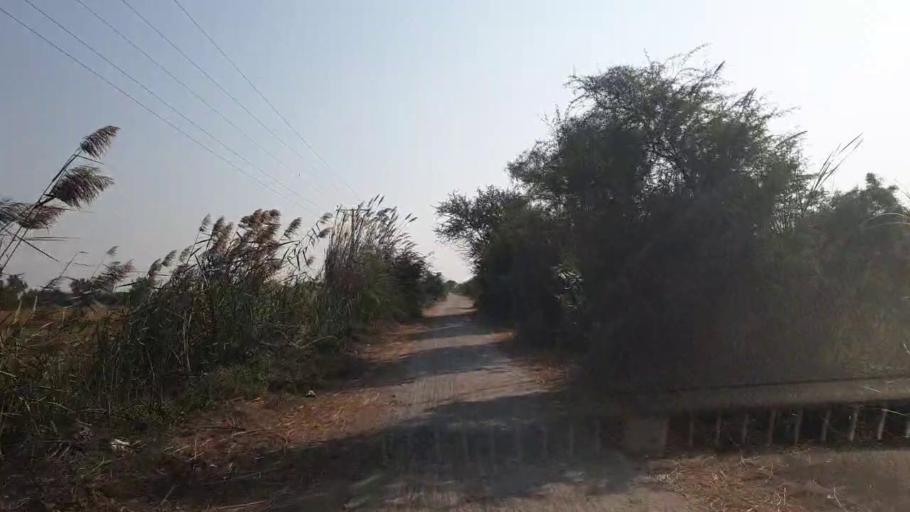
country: PK
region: Sindh
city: Kario
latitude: 24.8960
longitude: 68.6475
